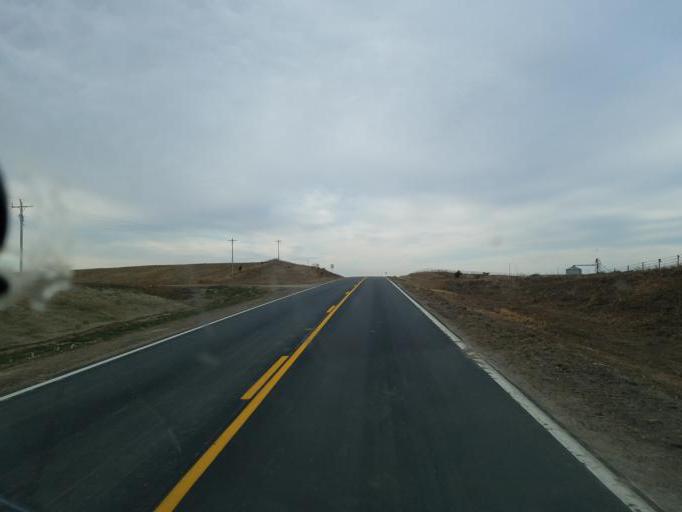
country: US
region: Nebraska
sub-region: Knox County
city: Center
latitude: 42.5971
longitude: -97.7925
